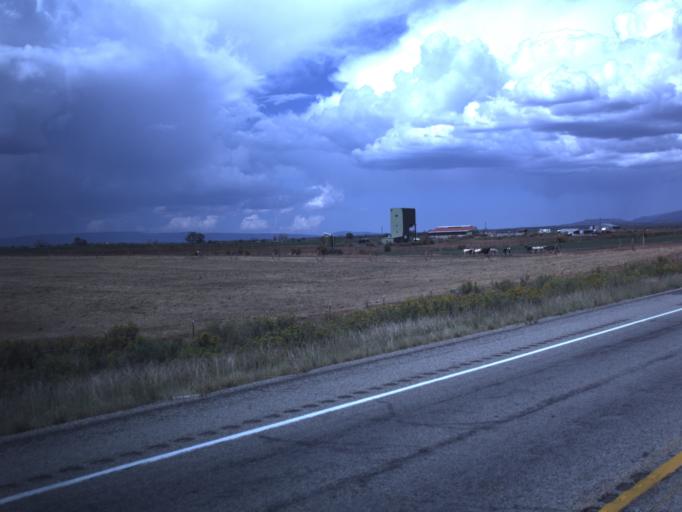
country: US
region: Utah
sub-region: San Juan County
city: Blanding
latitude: 37.5679
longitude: -109.4894
